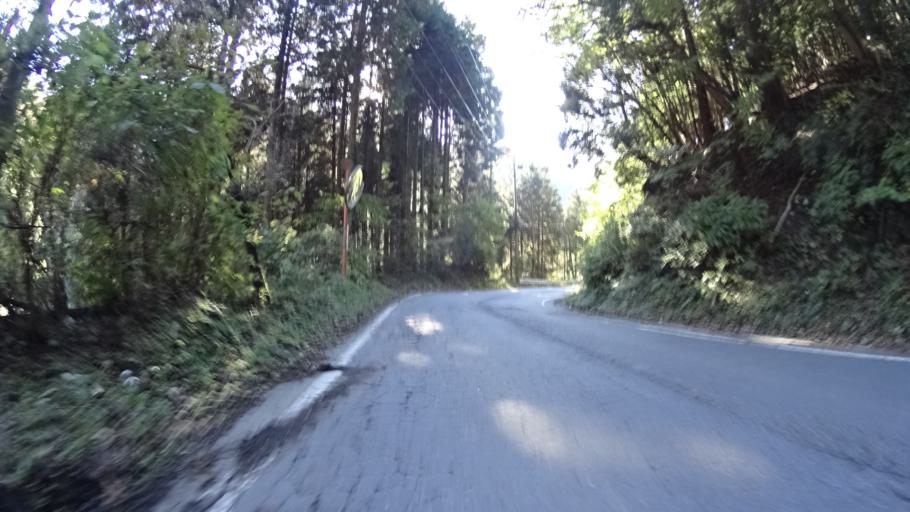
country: JP
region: Yamanashi
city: Uenohara
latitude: 35.6832
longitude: 139.0982
